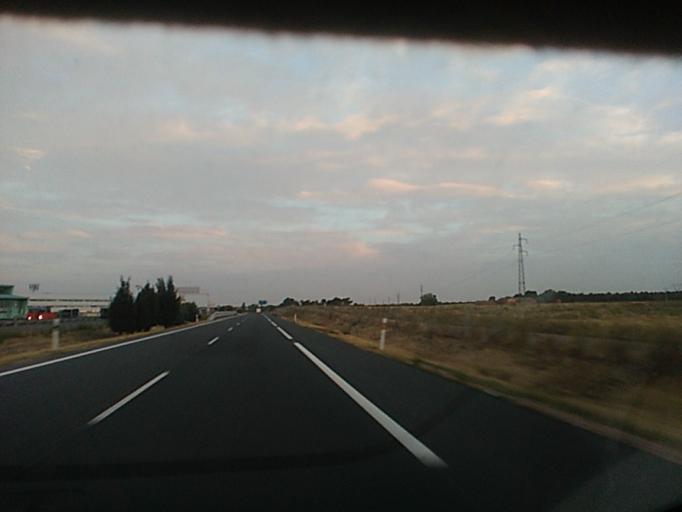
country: ES
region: Castille and Leon
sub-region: Provincia de Avila
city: Arevalo
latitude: 41.0764
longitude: -4.7273
